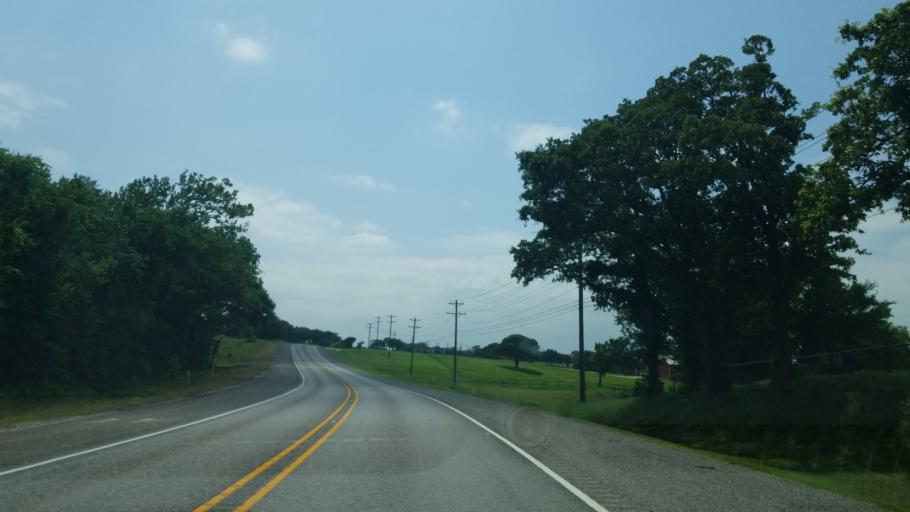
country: US
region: Texas
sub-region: Denton County
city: Aubrey
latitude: 33.3047
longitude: -97.0094
